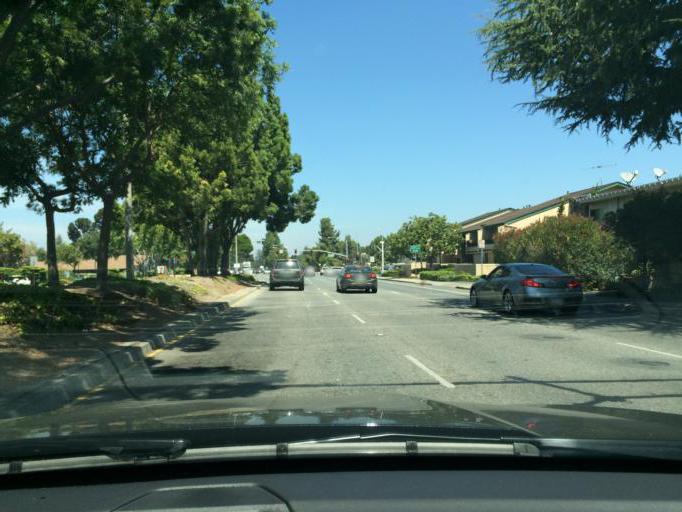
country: US
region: California
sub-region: Santa Clara County
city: Sunnyvale
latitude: 37.3576
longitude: -122.0322
